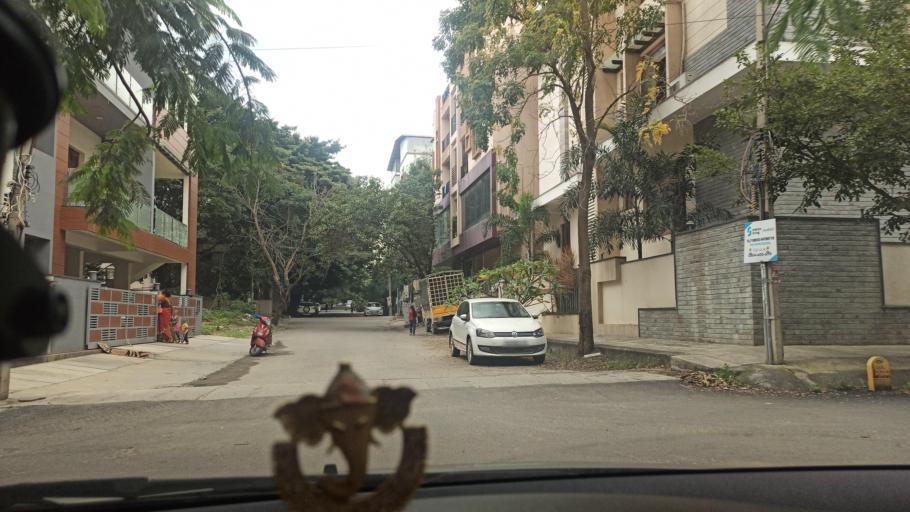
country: IN
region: Karnataka
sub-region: Bangalore Urban
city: Bangalore
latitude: 12.9151
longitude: 77.6471
